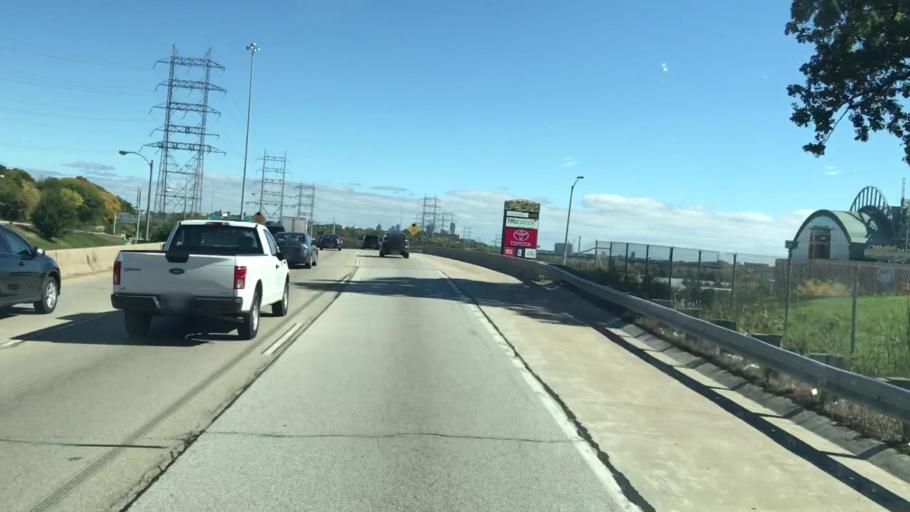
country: US
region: Wisconsin
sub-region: Milwaukee County
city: West Milwaukee
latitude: 43.0306
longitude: -87.9794
